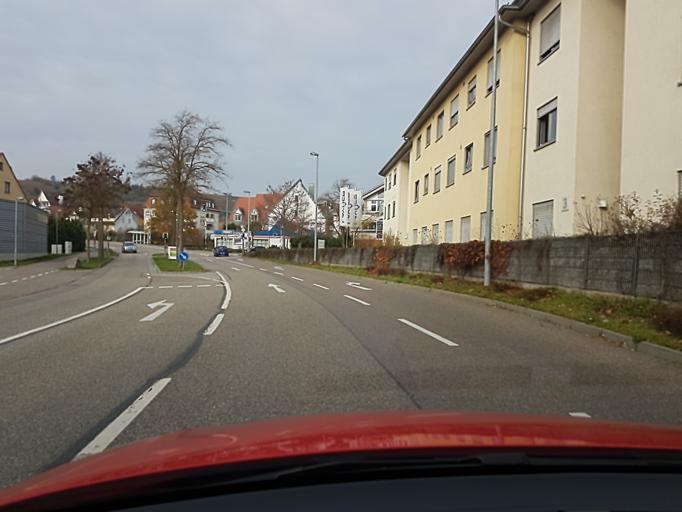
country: DE
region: Baden-Wuerttemberg
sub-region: Regierungsbezirk Stuttgart
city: Besigheim
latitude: 48.9968
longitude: 9.1412
